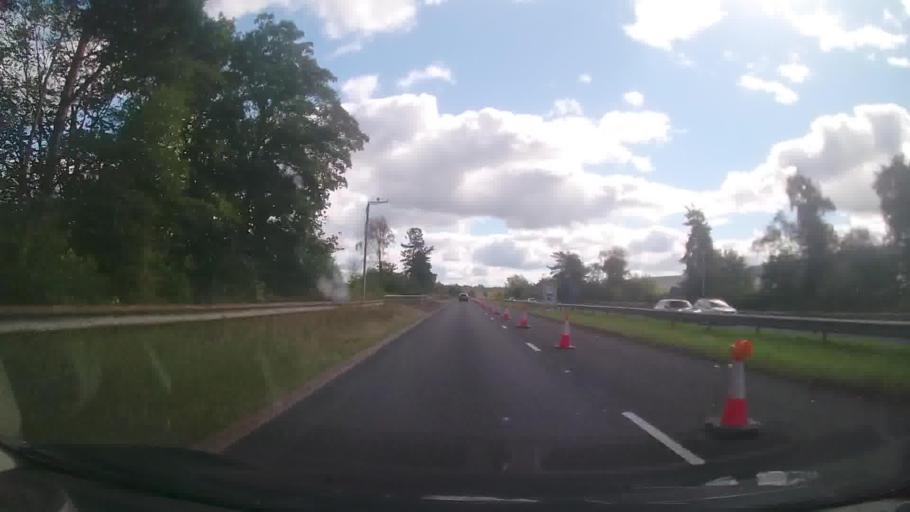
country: GB
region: Wales
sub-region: Rhondda Cynon Taf
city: Hirwaun
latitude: 51.7460
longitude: -3.5359
